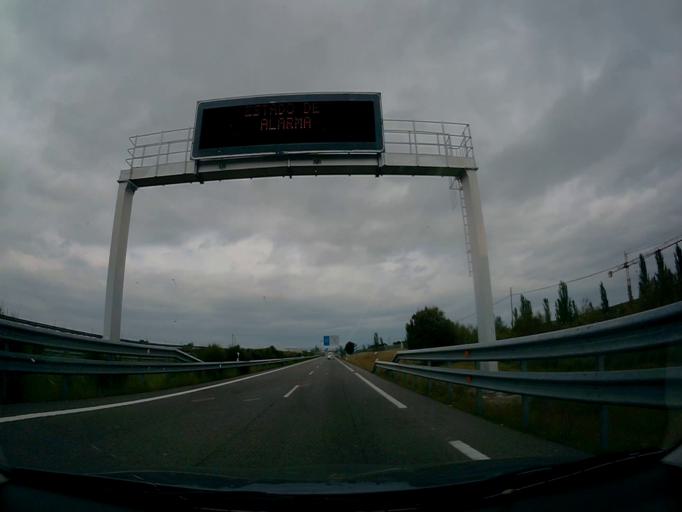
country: ES
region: Madrid
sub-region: Provincia de Madrid
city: Brunete
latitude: 40.3880
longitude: -3.9820
